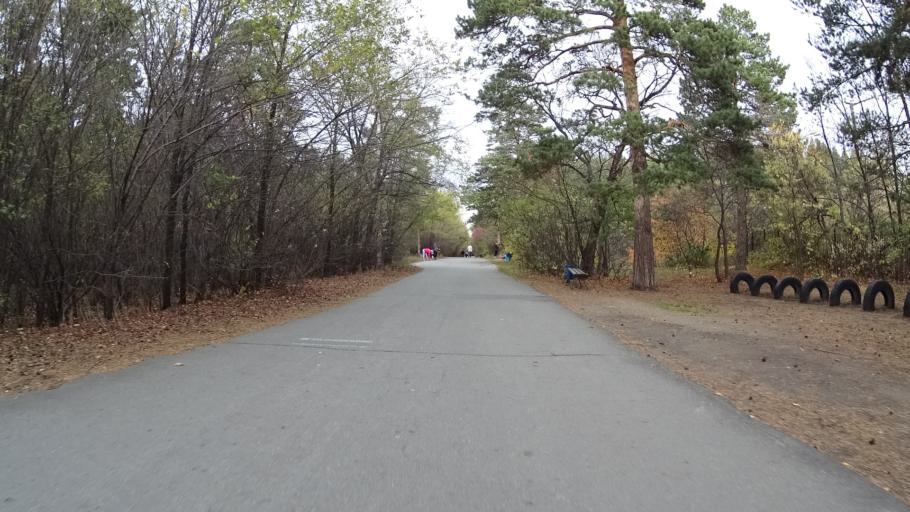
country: RU
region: Chelyabinsk
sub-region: Gorod Chelyabinsk
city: Chelyabinsk
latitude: 55.1489
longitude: 61.3555
